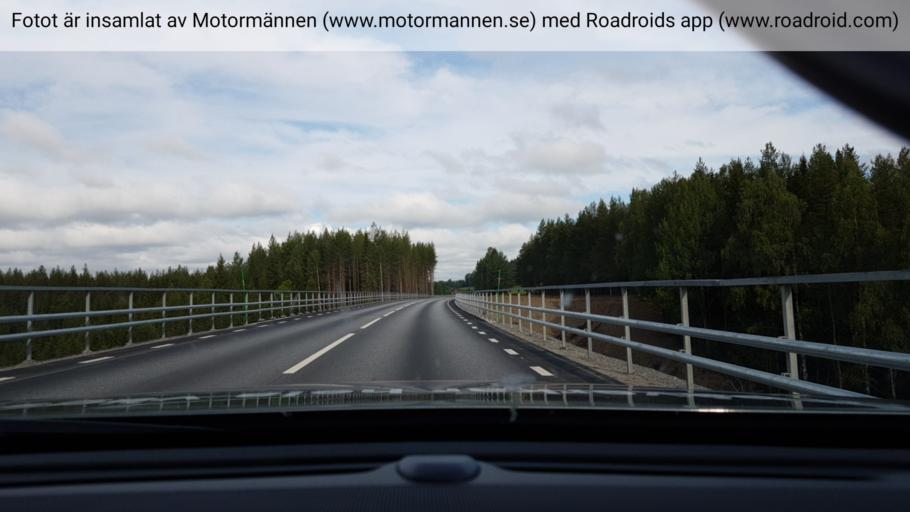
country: SE
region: Vaesterbotten
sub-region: Vindelns Kommun
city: Vindeln
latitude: 64.1749
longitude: 19.7375
